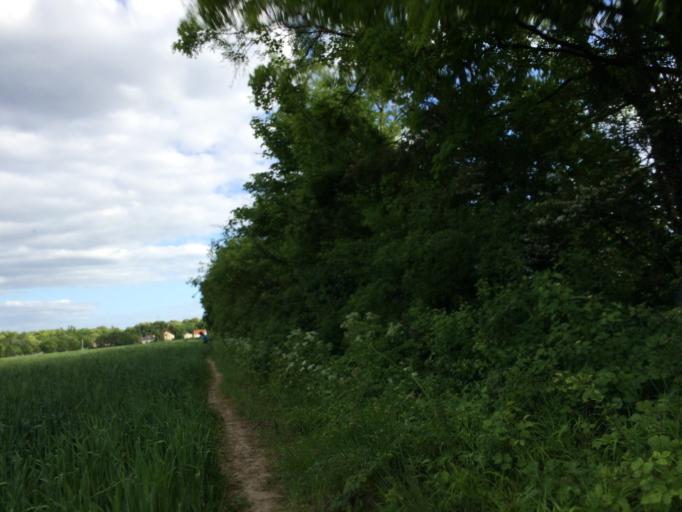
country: FR
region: Ile-de-France
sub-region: Departement de l'Essonne
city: Ris-Orangis
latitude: 48.6659
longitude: 2.4114
